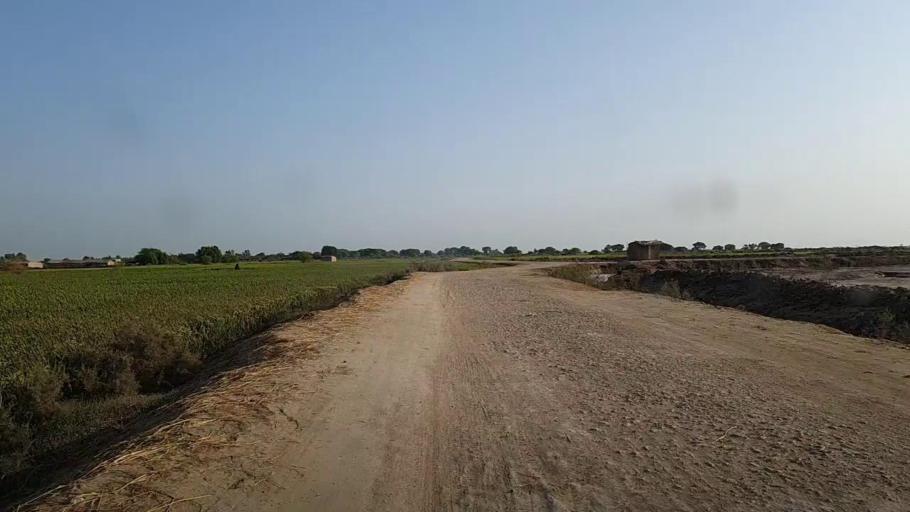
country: PK
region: Sindh
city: Bulri
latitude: 24.7438
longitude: 68.4220
